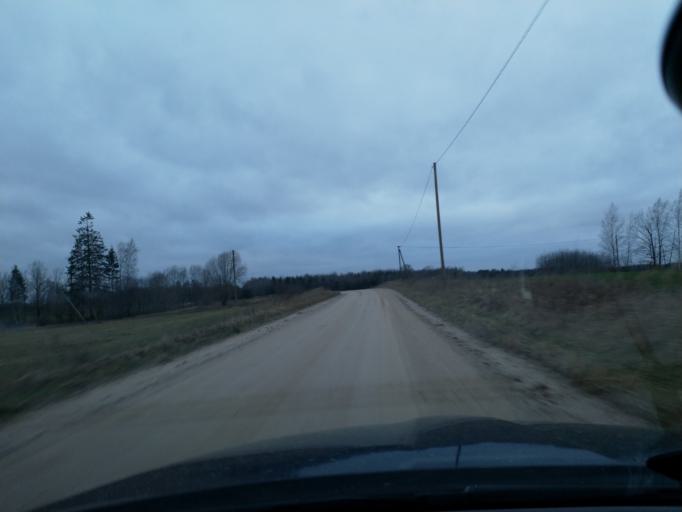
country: LV
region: Saldus Rajons
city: Saldus
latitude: 56.8969
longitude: 22.3030
